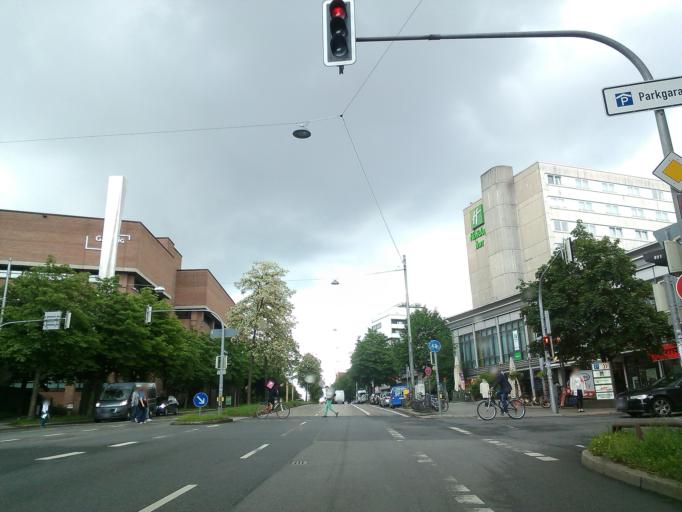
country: DE
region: Bavaria
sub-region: Upper Bavaria
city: Munich
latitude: 48.1313
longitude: 11.5899
